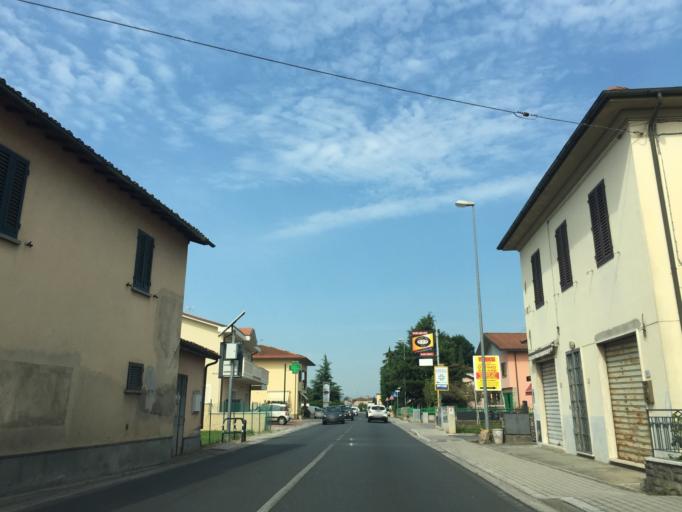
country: IT
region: Tuscany
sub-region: Provincia di Pistoia
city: Margine Coperta-Traversagna
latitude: 43.8709
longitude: 10.7604
